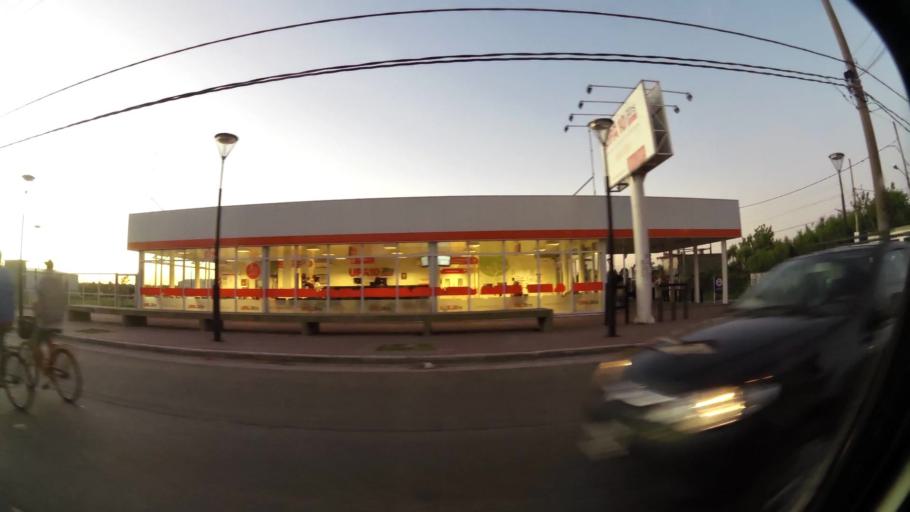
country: AR
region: Buenos Aires
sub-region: Partido de Quilmes
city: Quilmes
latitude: -34.8001
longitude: -58.1744
